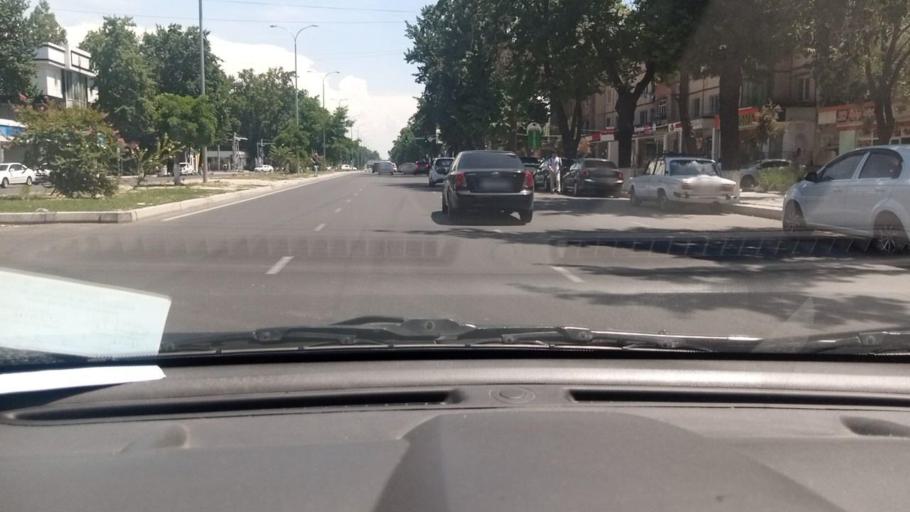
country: UZ
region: Toshkent Shahri
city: Tashkent
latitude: 41.2873
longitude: 69.2041
